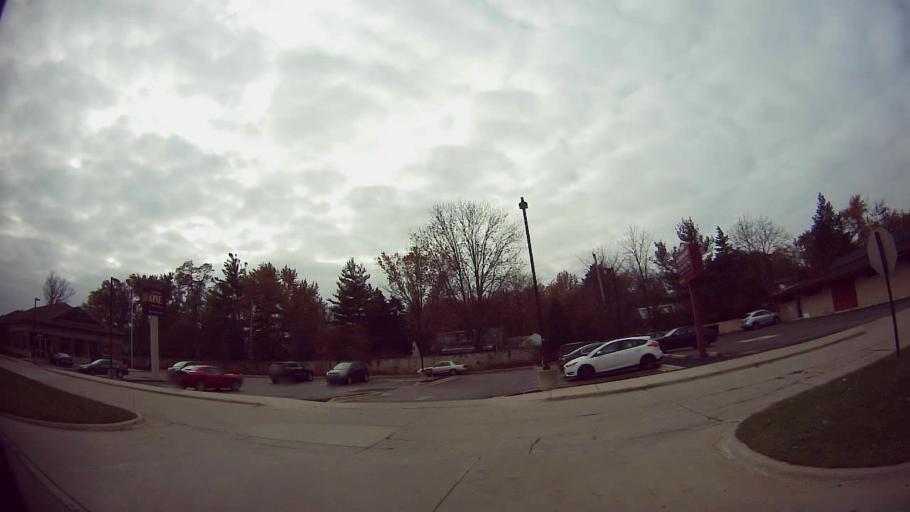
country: US
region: Michigan
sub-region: Oakland County
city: Berkley
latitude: 42.4998
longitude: -83.1689
